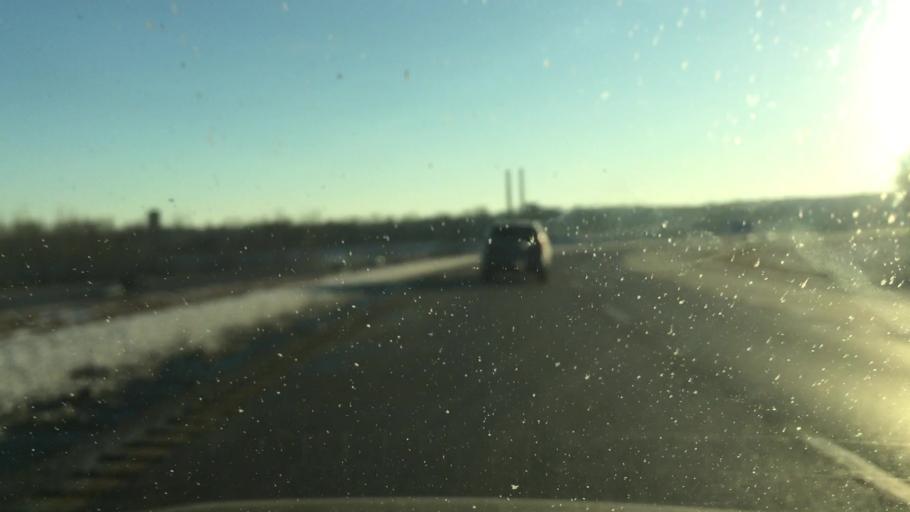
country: US
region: Missouri
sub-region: Platte County
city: Riverside
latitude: 39.1632
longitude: -94.6276
